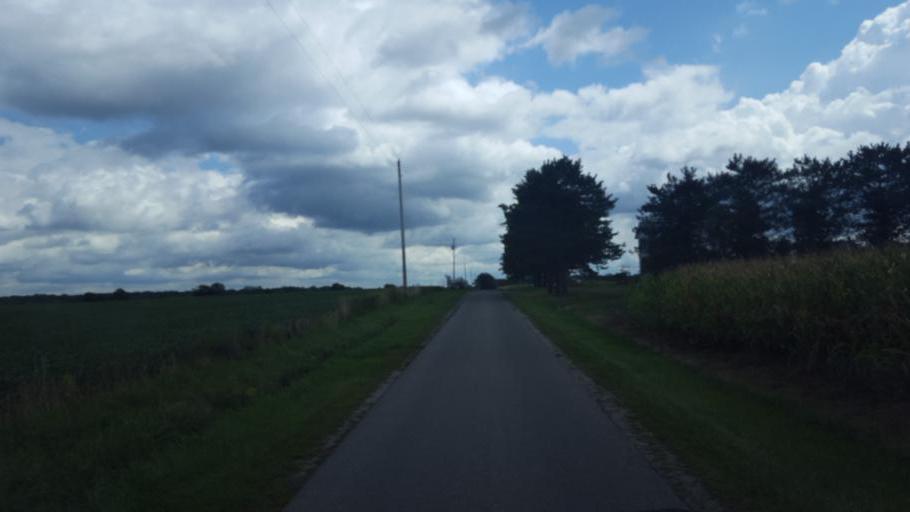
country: US
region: Ohio
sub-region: Huron County
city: Willard
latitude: 41.1151
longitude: -82.7621
